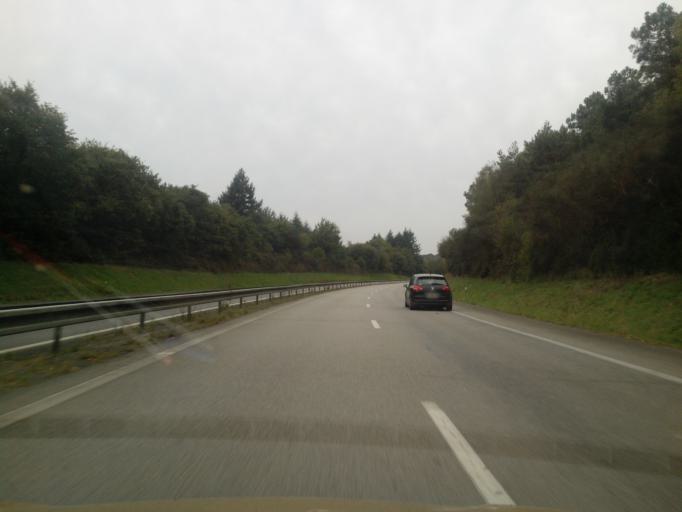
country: FR
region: Brittany
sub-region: Departement du Morbihan
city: Baud
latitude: 47.8743
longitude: -3.0523
